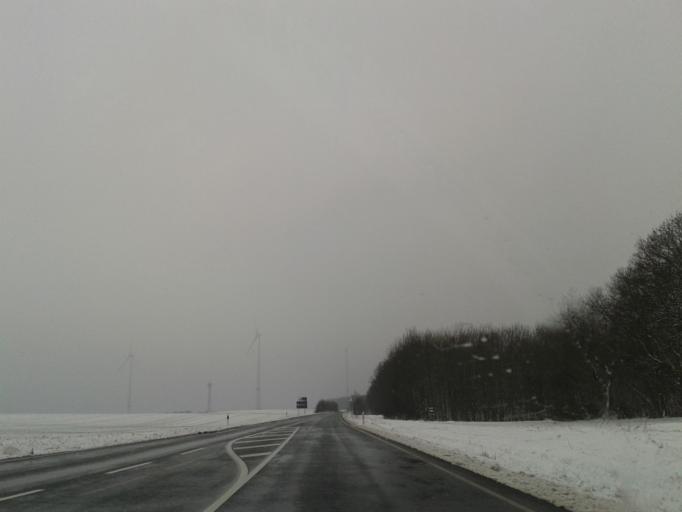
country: DE
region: Bavaria
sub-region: Regierungsbezirk Unterfranken
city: Gadheim
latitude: 50.0403
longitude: 10.3668
